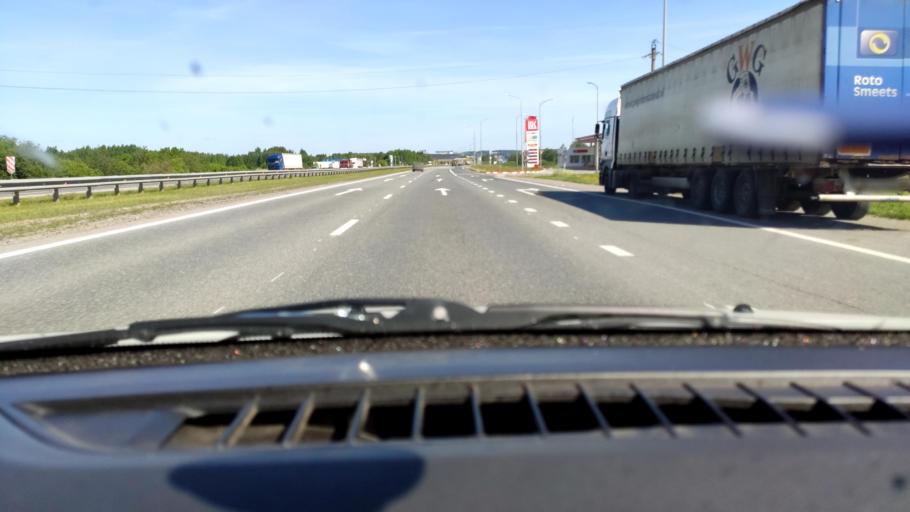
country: RU
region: Perm
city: Froly
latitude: 57.8988
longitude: 56.2662
